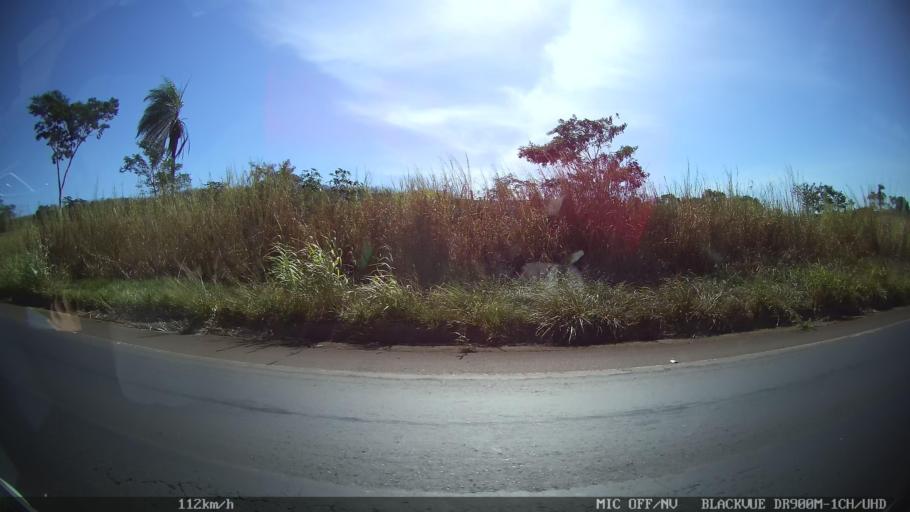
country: BR
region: Sao Paulo
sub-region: Olimpia
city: Olimpia
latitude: -20.6171
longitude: -48.7620
